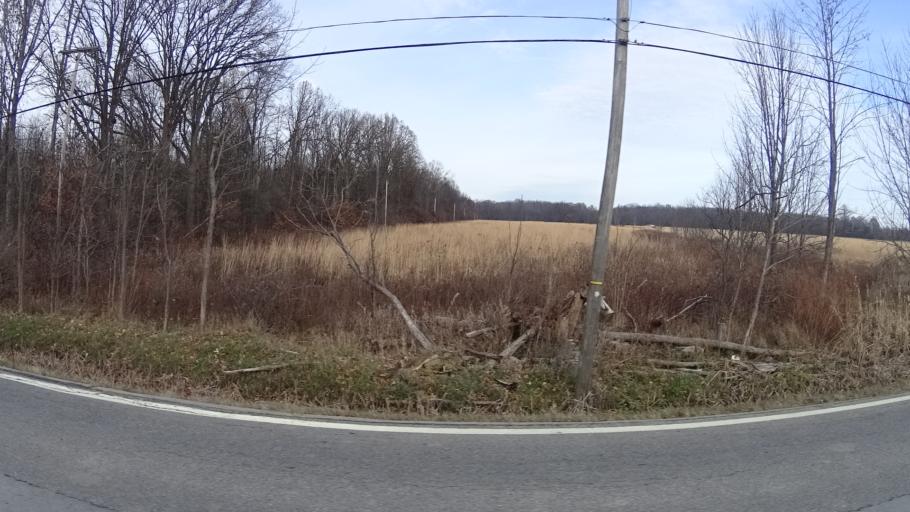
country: US
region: Ohio
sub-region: Lorain County
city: Eaton Estates
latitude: 41.2373
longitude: -81.9801
